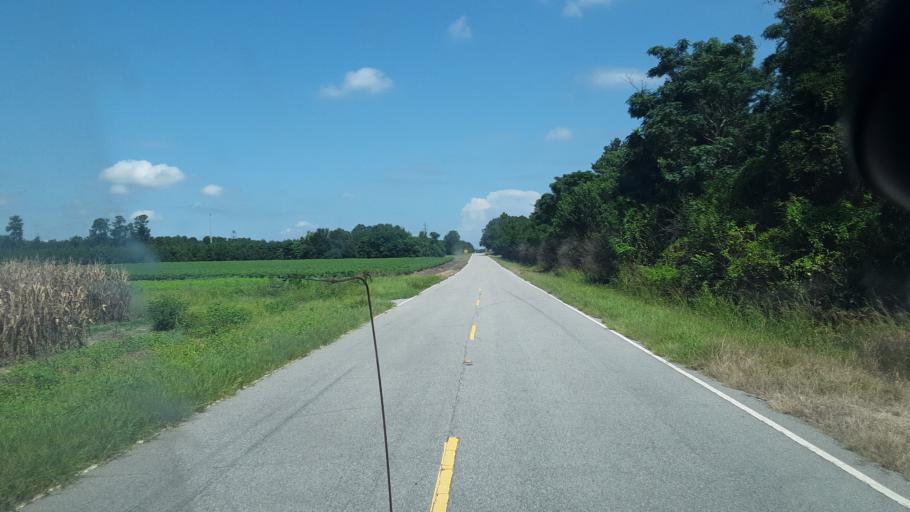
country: US
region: South Carolina
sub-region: Bamberg County
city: Bamberg
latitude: 33.4019
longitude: -81.0155
